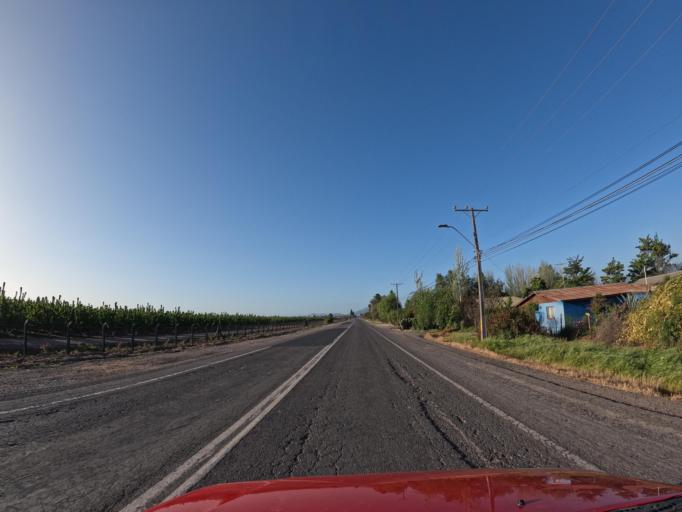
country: CL
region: O'Higgins
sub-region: Provincia de Colchagua
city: Santa Cruz
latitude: -34.5148
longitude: -71.3641
